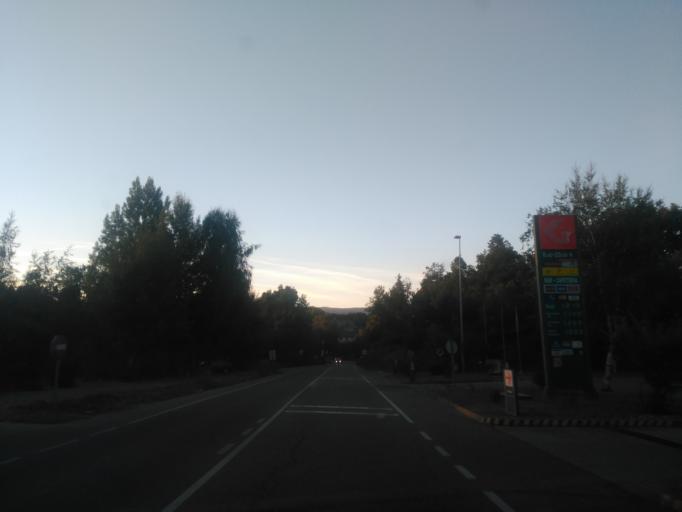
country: ES
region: Castille and Leon
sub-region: Provincia de Zamora
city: Puebla de Sanabria
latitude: 42.0812
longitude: -6.6405
